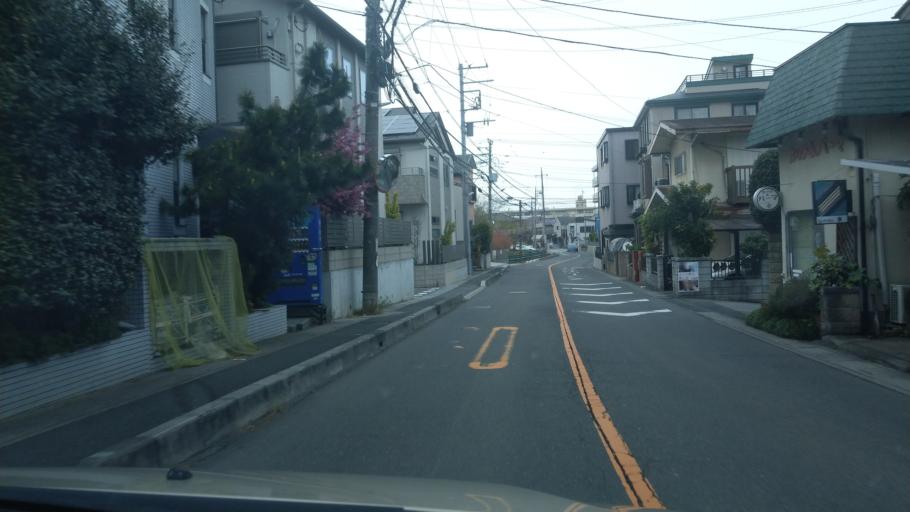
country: JP
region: Saitama
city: Ageoshimo
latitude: 35.9518
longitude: 139.5988
